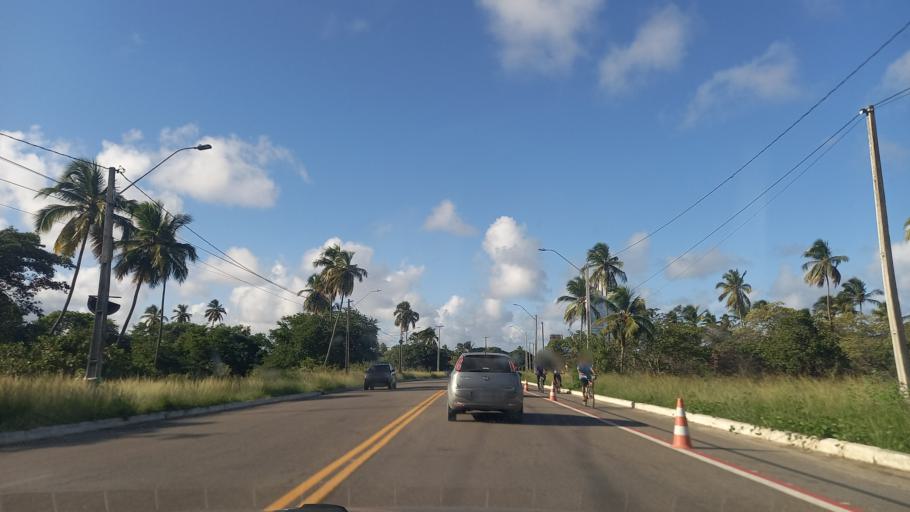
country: BR
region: Pernambuco
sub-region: Jaboatao Dos Guararapes
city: Jaboatao
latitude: -8.2315
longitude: -34.9358
